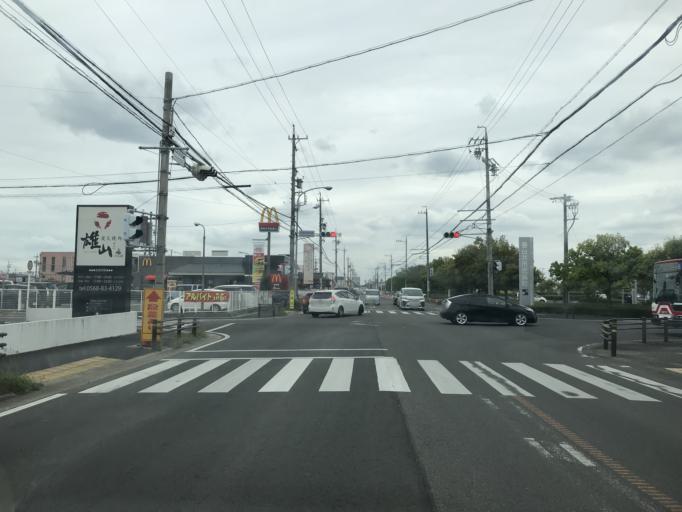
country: JP
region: Aichi
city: Kasugai
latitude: 35.2729
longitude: 136.9717
